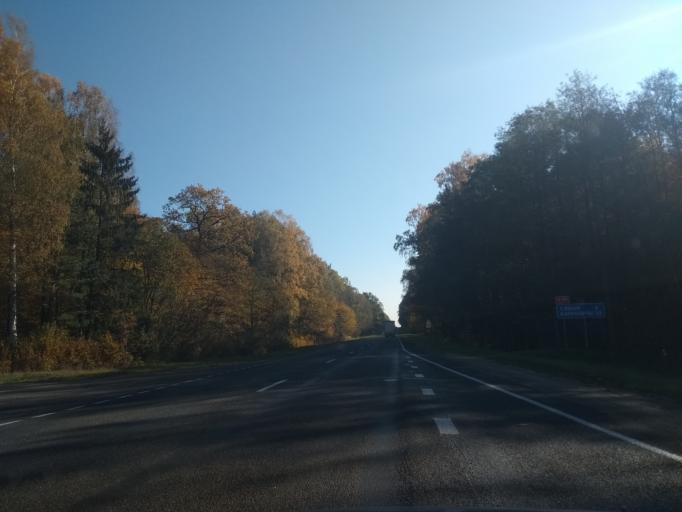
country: BY
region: Grodnenskaya
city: Slonim
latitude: 53.1095
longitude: 25.1747
